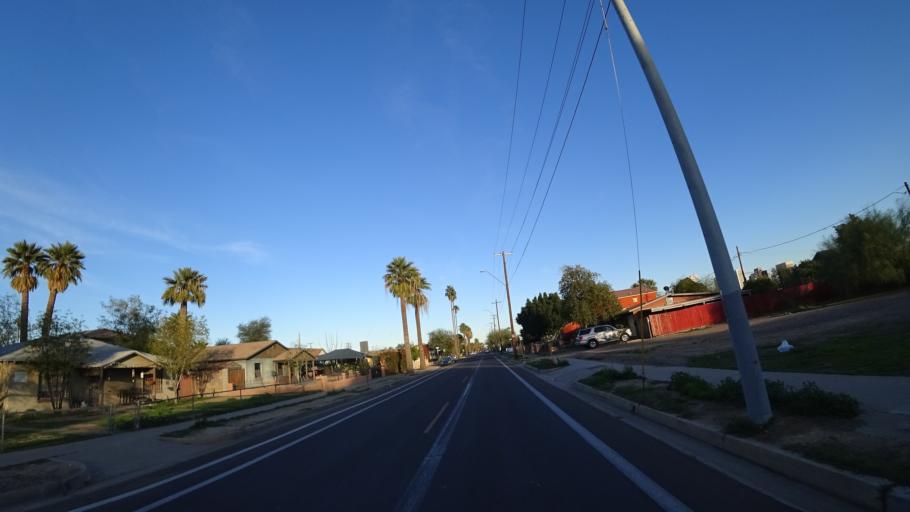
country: US
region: Arizona
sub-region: Maricopa County
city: Phoenix
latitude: 33.4586
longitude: -112.0881
